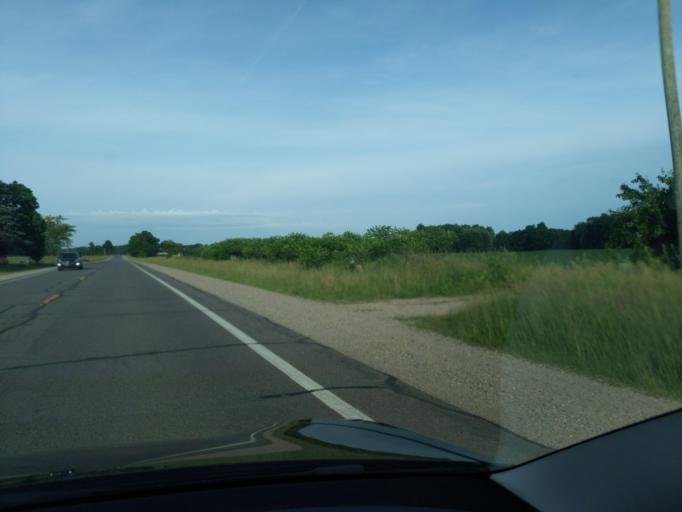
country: US
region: Michigan
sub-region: Montcalm County
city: Lakeview
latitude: 43.4322
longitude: -85.3731
